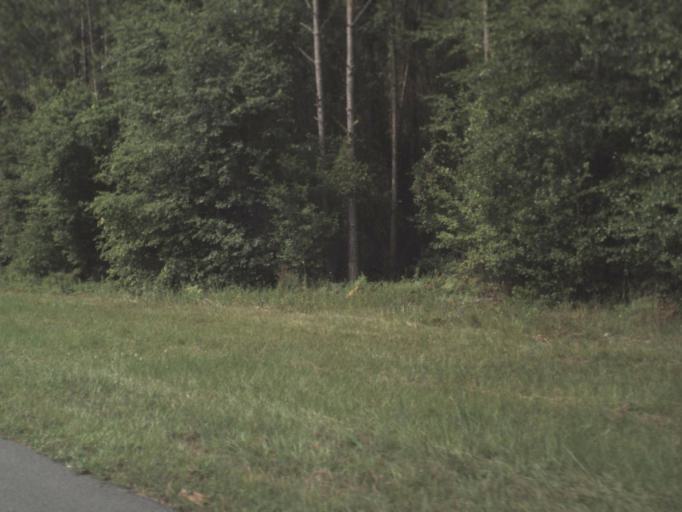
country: US
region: Florida
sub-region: Columbia County
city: Five Points
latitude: 30.3990
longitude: -82.6314
